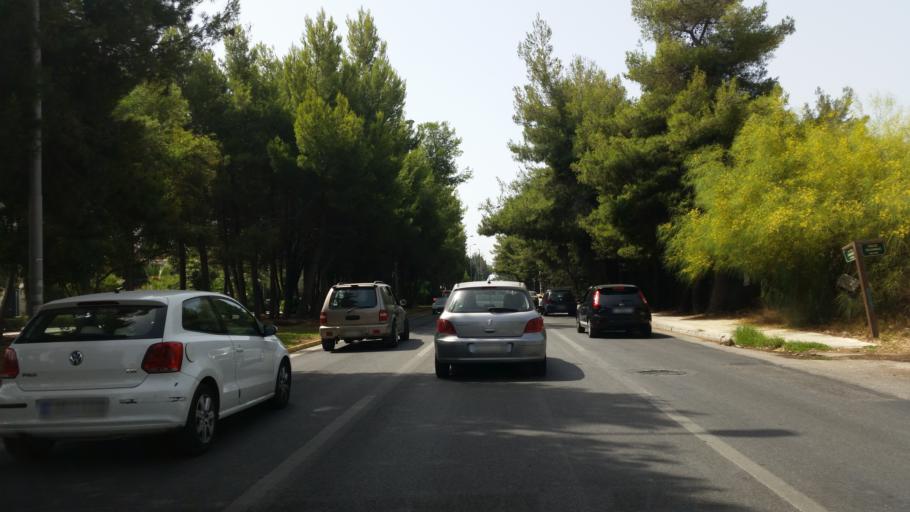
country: GR
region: Attica
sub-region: Nomarchia Anatolikis Attikis
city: Vouliagmeni
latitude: 37.8274
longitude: 23.7739
